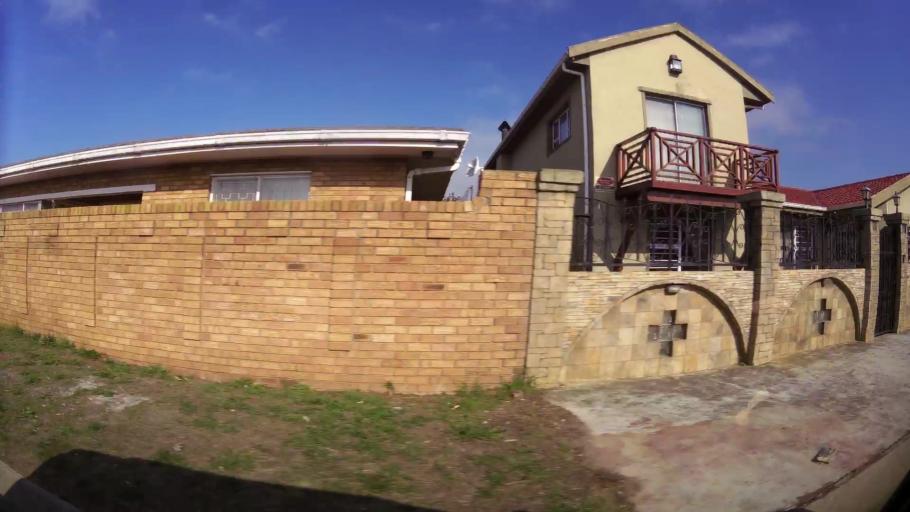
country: ZA
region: Eastern Cape
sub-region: Nelson Mandela Bay Metropolitan Municipality
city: Port Elizabeth
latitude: -33.9231
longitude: 25.5314
